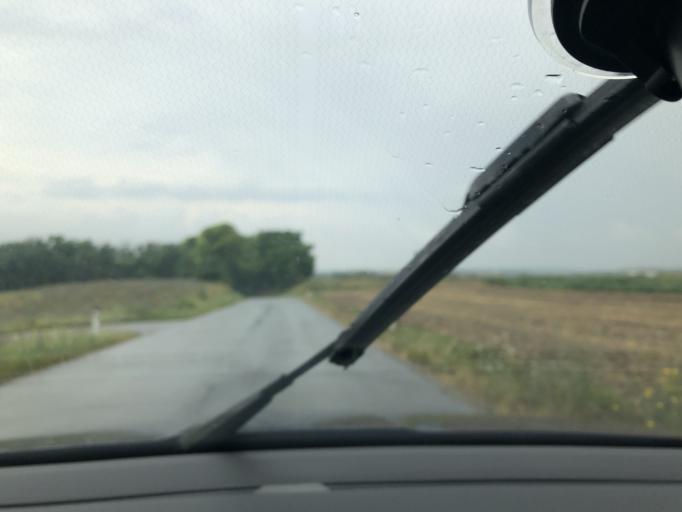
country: AT
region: Lower Austria
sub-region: Politischer Bezirk Ganserndorf
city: Auersthal
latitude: 48.3789
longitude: 16.6470
